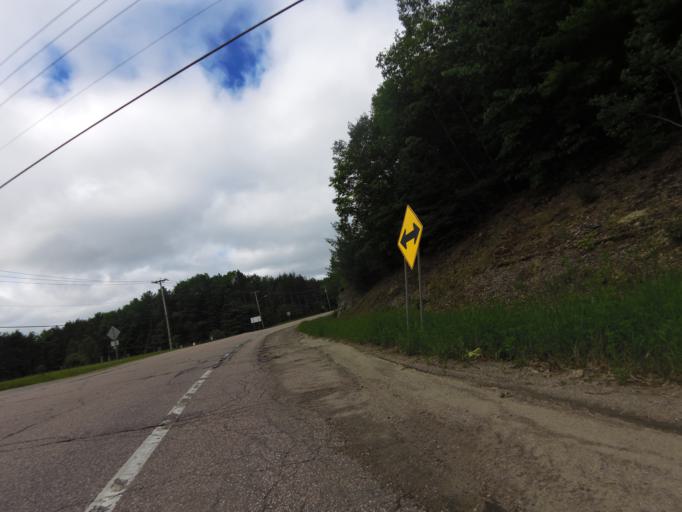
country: CA
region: Quebec
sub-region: Outaouais
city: Shawville
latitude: 45.8384
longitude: -76.4437
